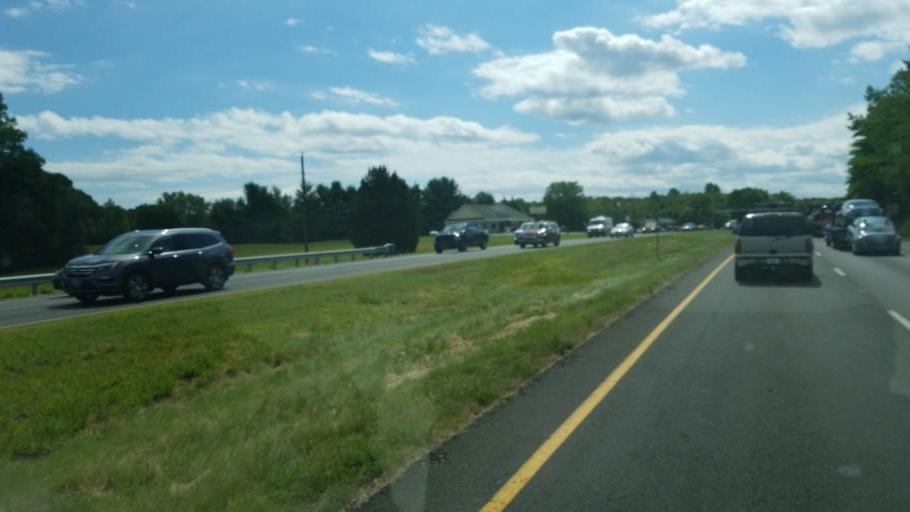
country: US
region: Virginia
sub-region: Fauquier County
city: Bealeton
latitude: 38.5014
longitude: -77.6948
